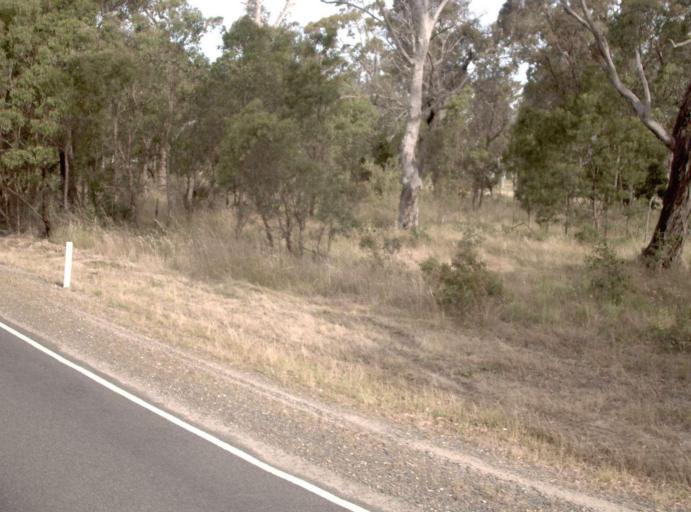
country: AU
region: Victoria
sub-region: Latrobe
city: Traralgon
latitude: -38.0594
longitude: 146.6341
